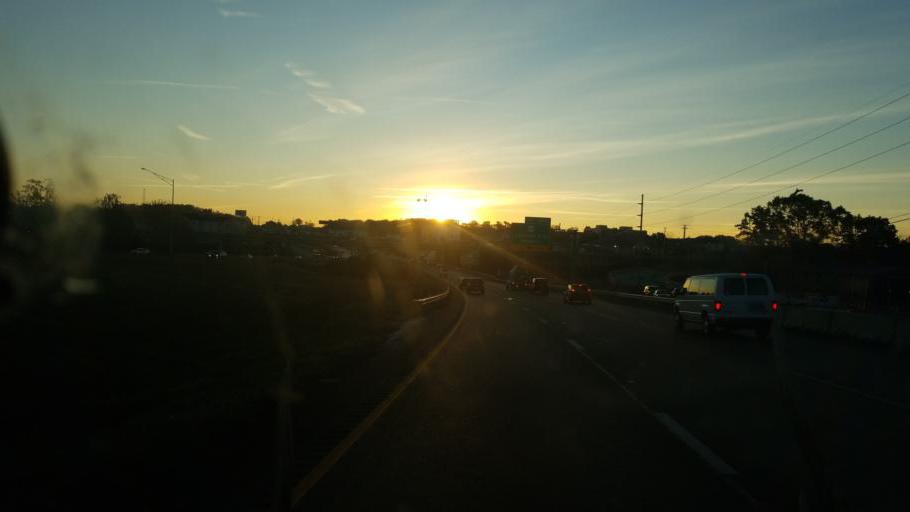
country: US
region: Missouri
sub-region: Boone County
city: Columbia
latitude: 38.9629
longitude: -92.2984
